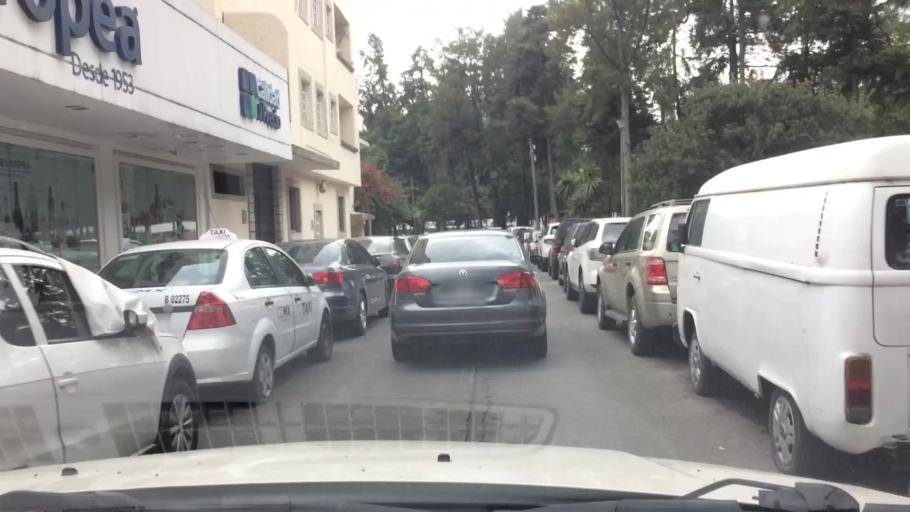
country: MX
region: Mexico City
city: Alvaro Obregon
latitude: 19.3486
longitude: -99.1865
